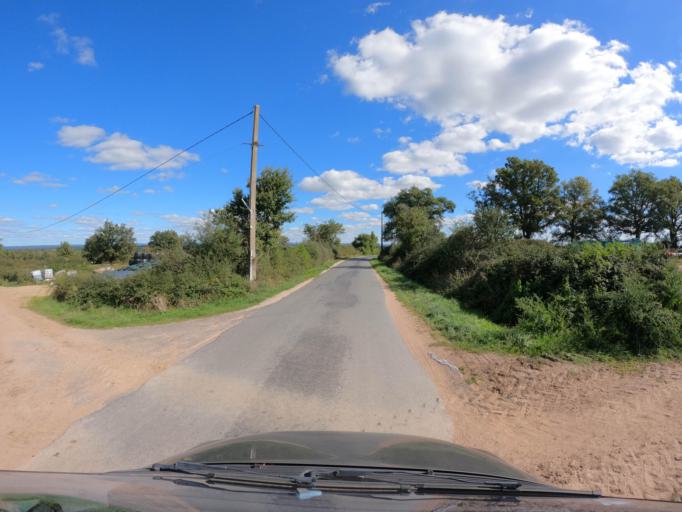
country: FR
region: Auvergne
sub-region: Departement de l'Allier
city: Doyet
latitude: 46.4004
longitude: 2.7473
